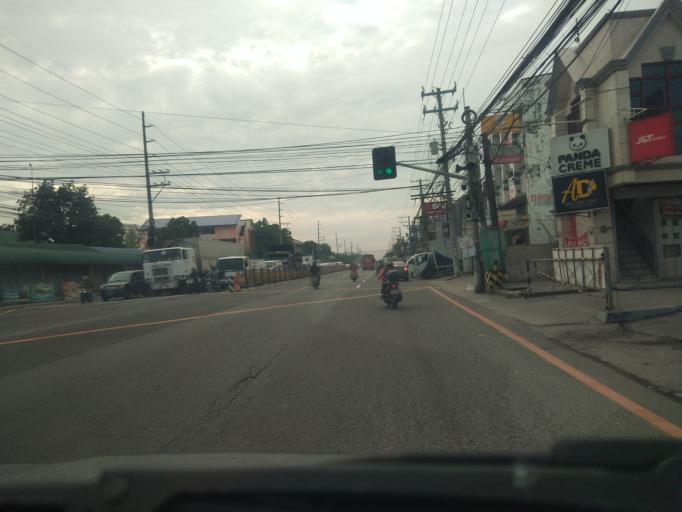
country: PH
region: Central Luzon
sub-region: Province of Pampanga
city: Bulaon
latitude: 15.0775
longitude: 120.6408
